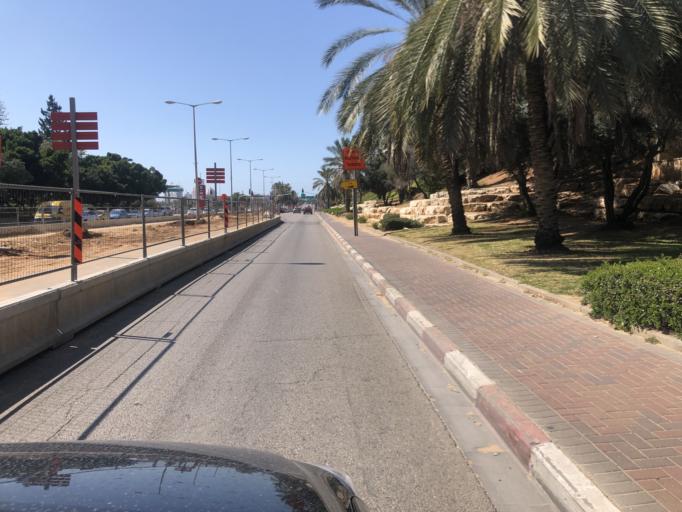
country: IL
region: Tel Aviv
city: Holon
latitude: 32.0011
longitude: 34.7659
